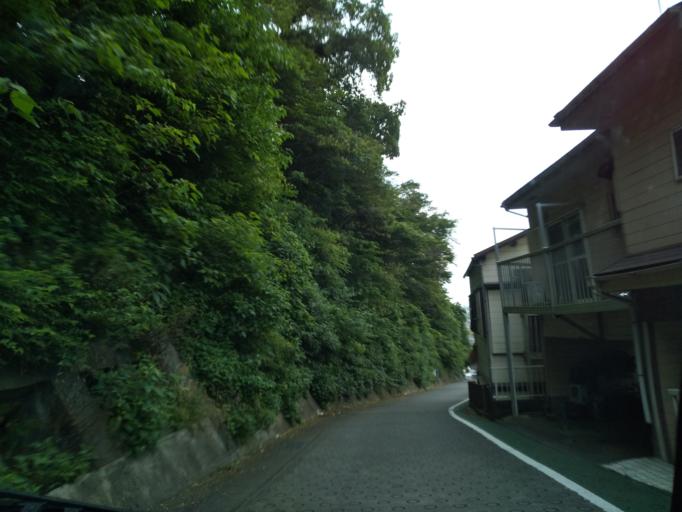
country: JP
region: Kanagawa
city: Zama
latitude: 35.5126
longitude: 139.3624
